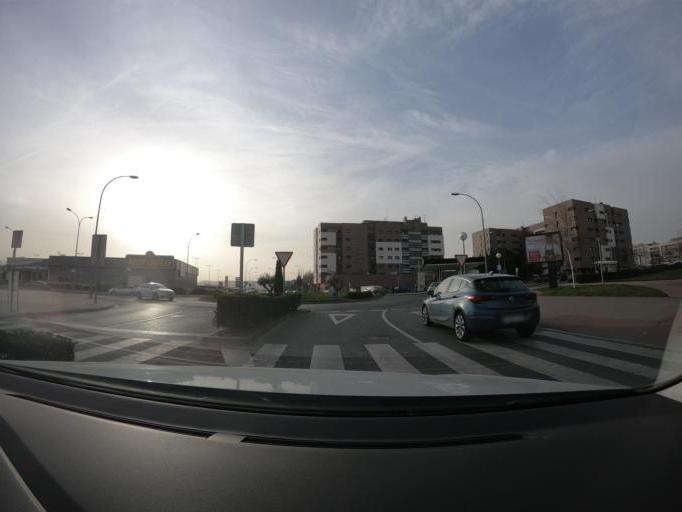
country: ES
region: La Rioja
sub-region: Provincia de La Rioja
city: Logrono
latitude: 42.4538
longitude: -2.4656
